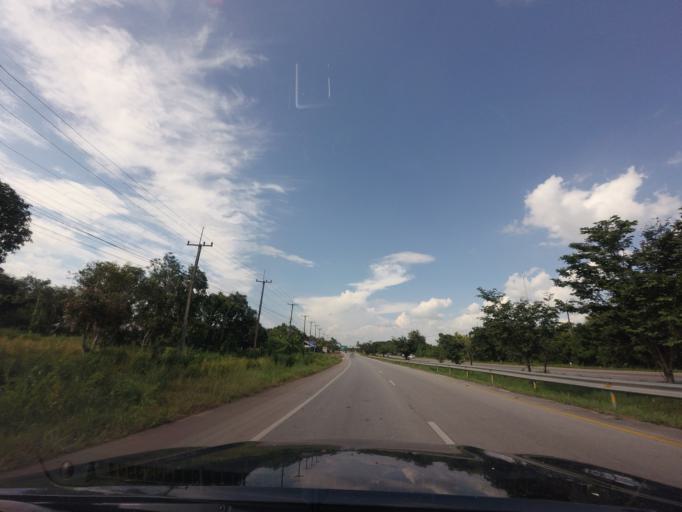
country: TH
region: Nong Khai
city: Sa Khrai
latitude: 17.6593
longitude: 102.7906
